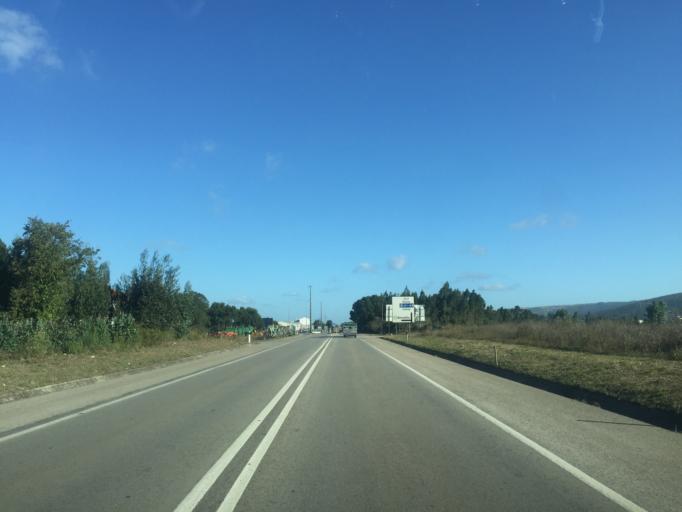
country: PT
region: Leiria
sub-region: Alcobaca
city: Benedita
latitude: 39.4221
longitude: -8.9618
